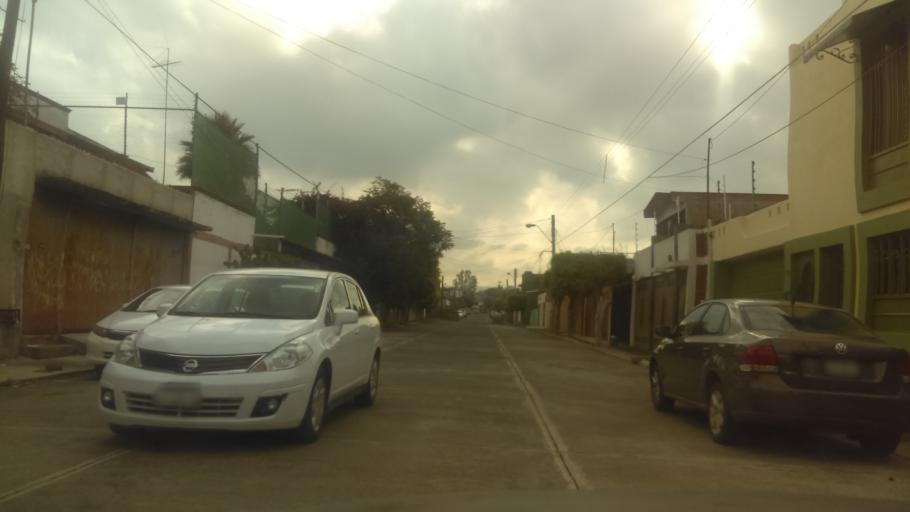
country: MX
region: Michoacan
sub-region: Morelia
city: Montana Monarca (Punta Altozano)
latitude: 19.6732
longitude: -101.1869
